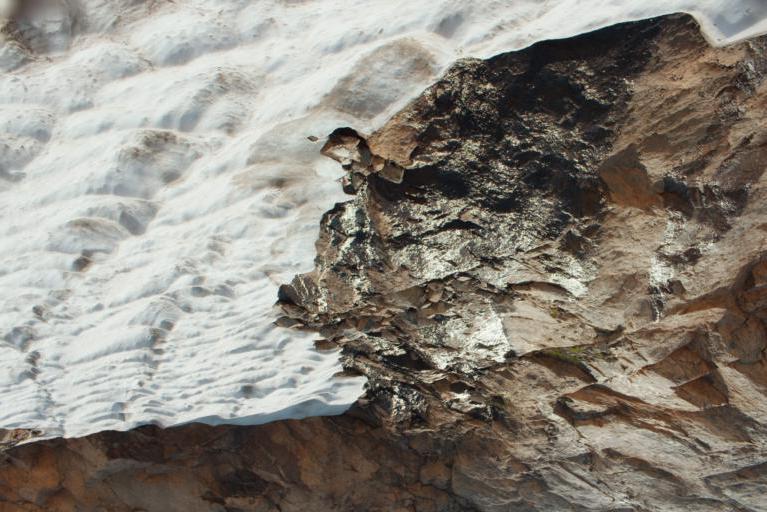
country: RU
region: Karachayevo-Cherkesiya
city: Nizhniy Arkhyz
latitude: 43.4575
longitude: 41.2201
